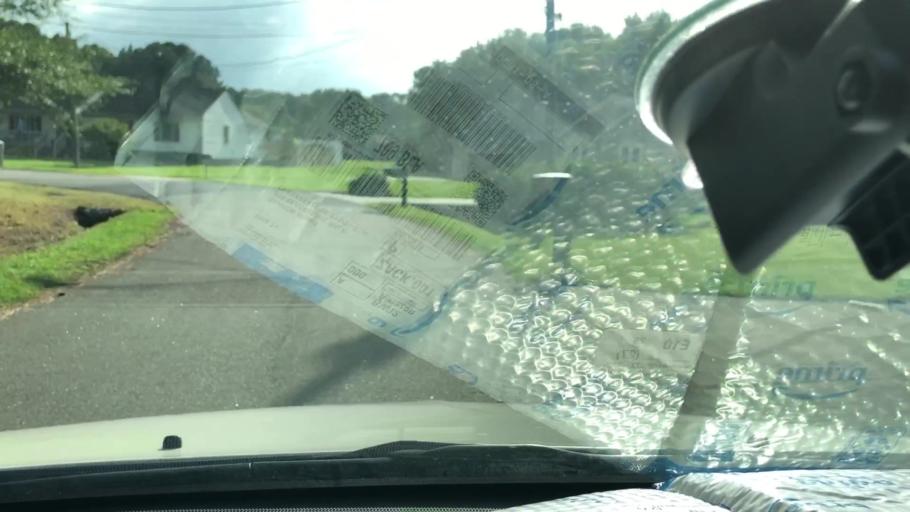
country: US
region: Virginia
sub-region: City of Chesapeake
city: Chesapeake
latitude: 36.7049
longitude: -76.2758
